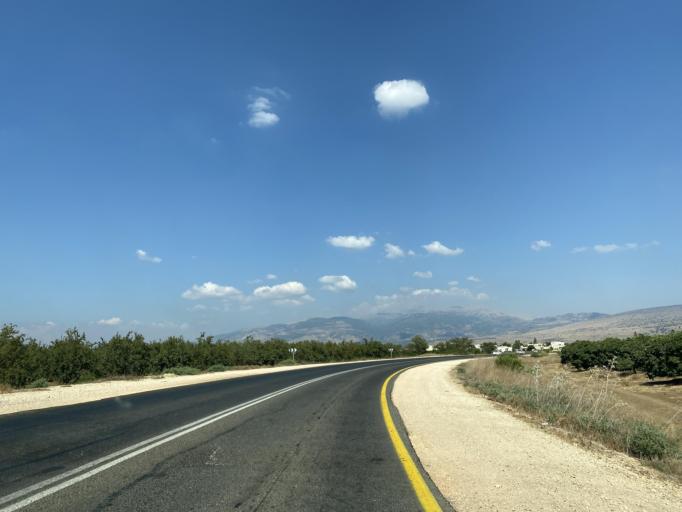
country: IL
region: Northern District
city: Qiryat Shemona
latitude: 33.1716
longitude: 35.5996
